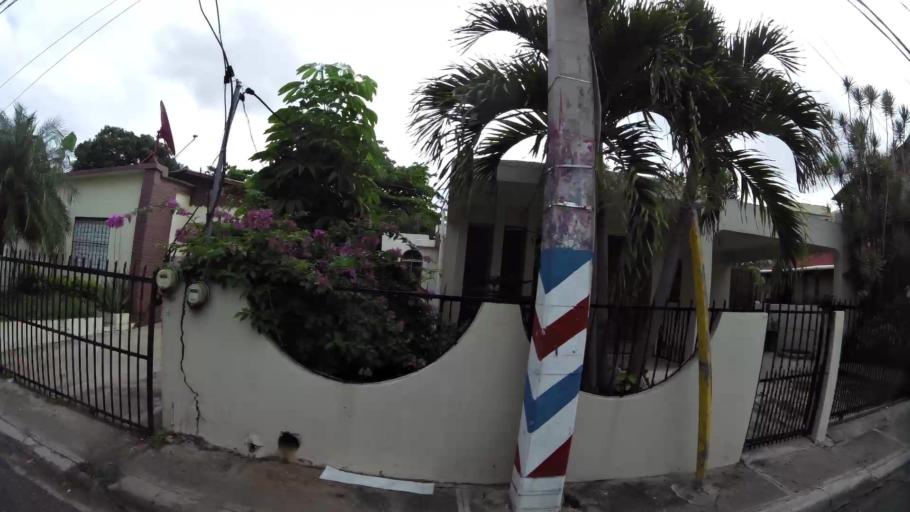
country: DO
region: Santiago
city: Santiago de los Caballeros
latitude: 19.4590
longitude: -70.6684
